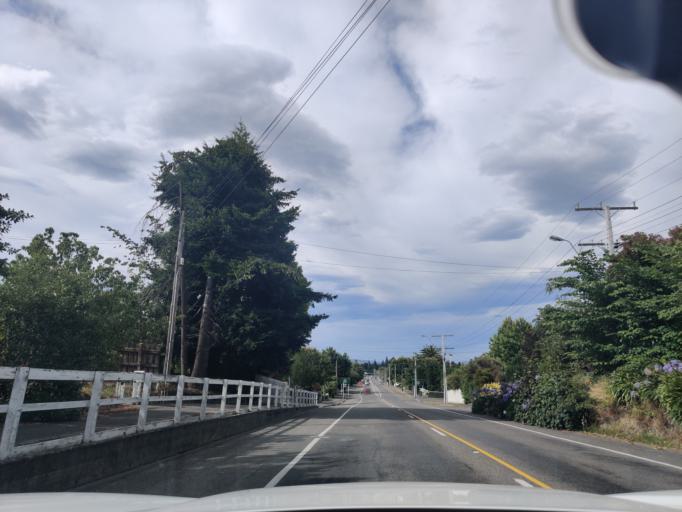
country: NZ
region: Wellington
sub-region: Masterton District
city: Masterton
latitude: -40.9369
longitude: 175.6709
